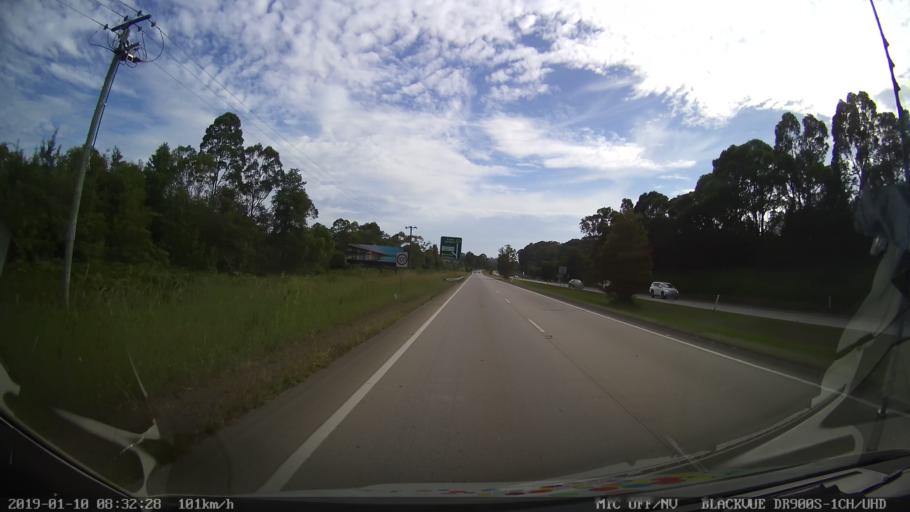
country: AU
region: New South Wales
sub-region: Coffs Harbour
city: Boambee
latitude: -30.3432
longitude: 153.0706
